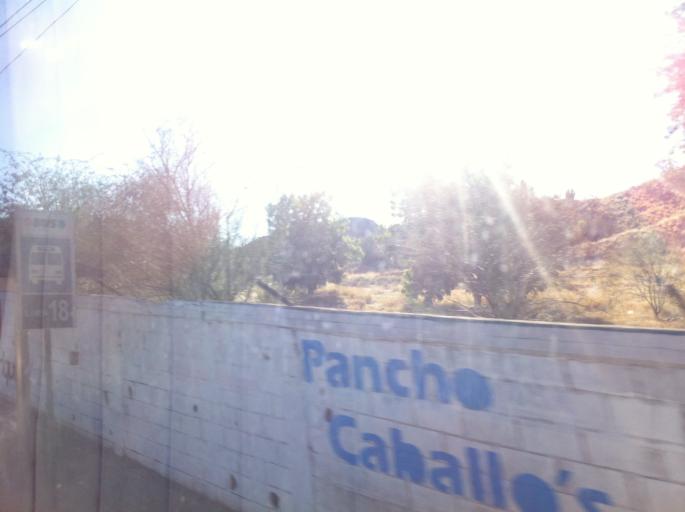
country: MX
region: Sonora
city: Hermosillo
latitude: 29.0933
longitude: -110.9313
